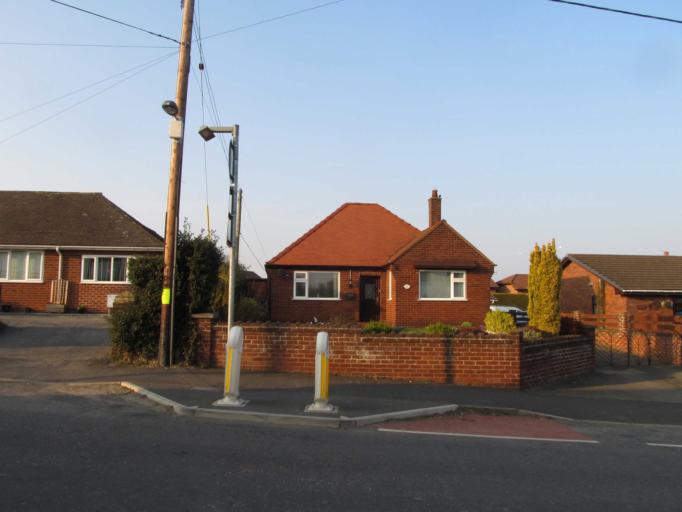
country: GB
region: Wales
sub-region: County of Flintshire
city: Buckley
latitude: 53.2017
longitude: -3.0907
